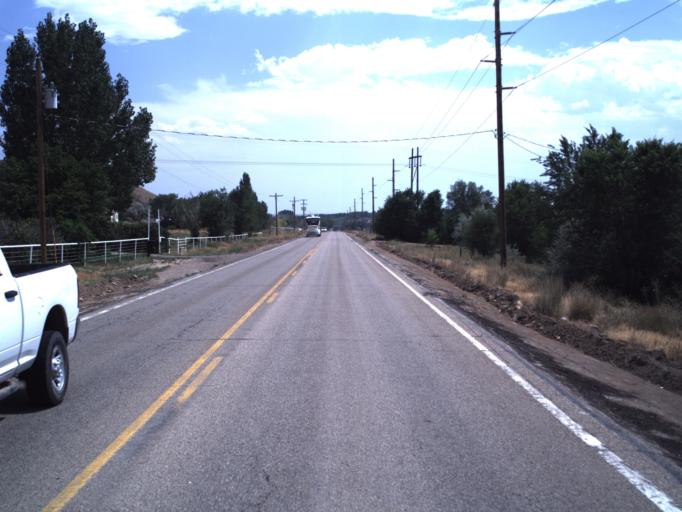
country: US
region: Utah
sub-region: Duchesne County
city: Roosevelt
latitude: 40.3299
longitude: -110.0198
